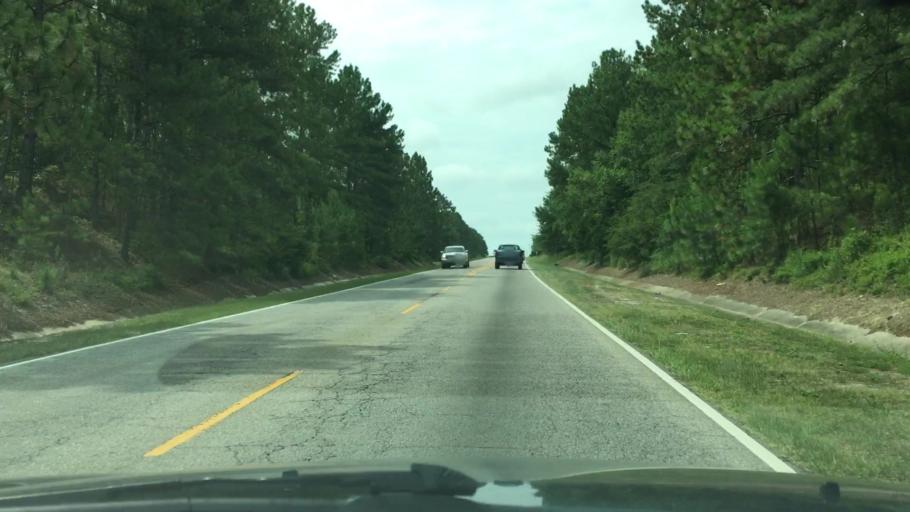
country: US
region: South Carolina
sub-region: Aiken County
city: Warrenville
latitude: 33.5503
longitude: -81.7775
